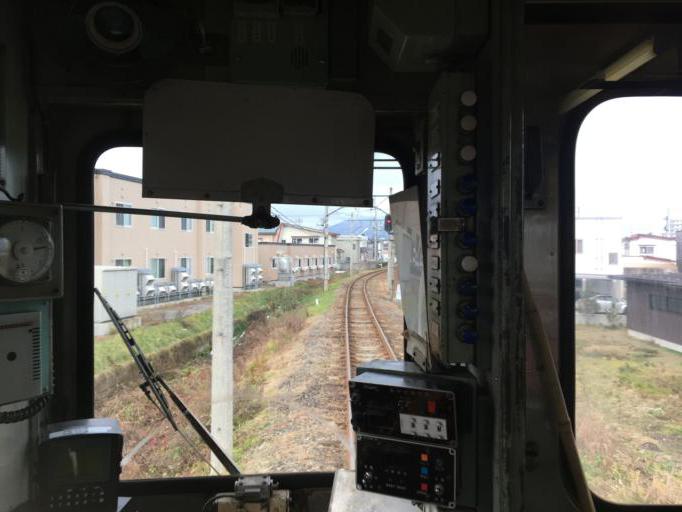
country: JP
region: Aomori
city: Hirosaki
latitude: 40.5658
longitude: 140.4824
